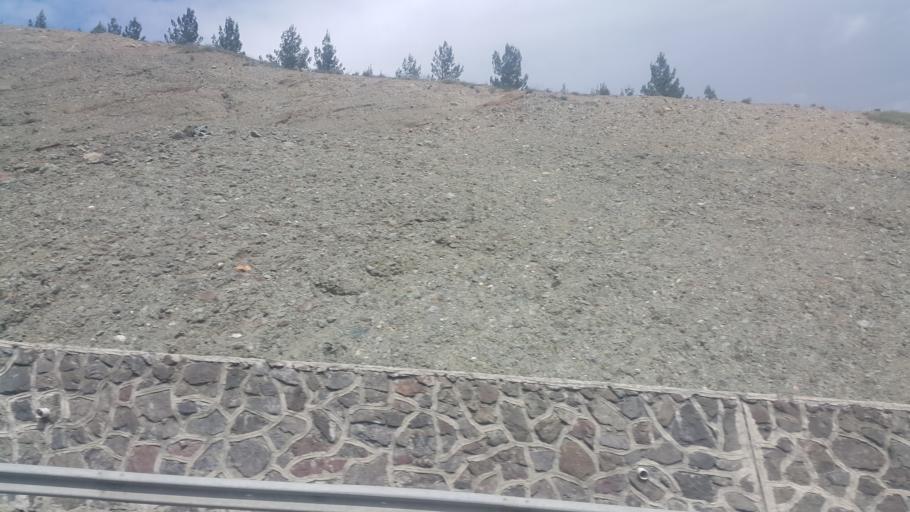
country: TR
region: Adana
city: Pozanti
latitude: 37.4509
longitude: 34.8814
